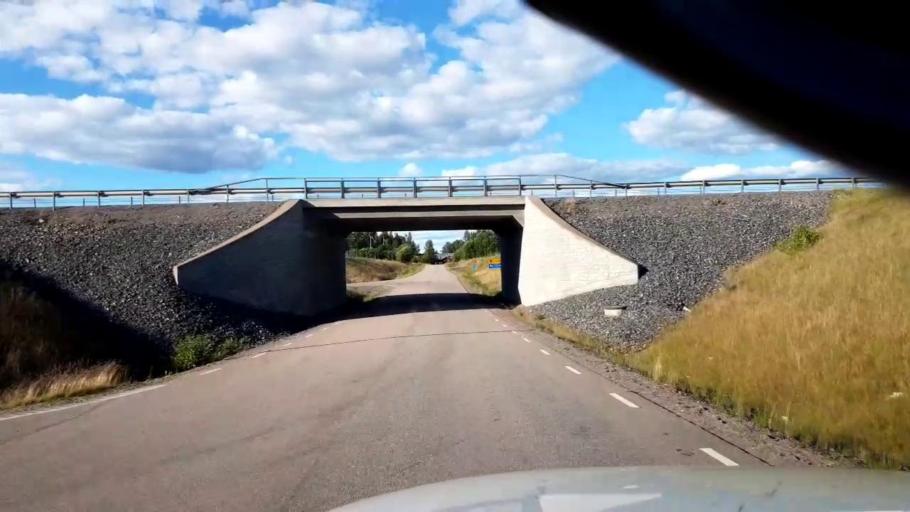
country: SE
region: Dalarna
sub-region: Borlange Kommun
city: Ornas
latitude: 60.4235
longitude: 15.5391
